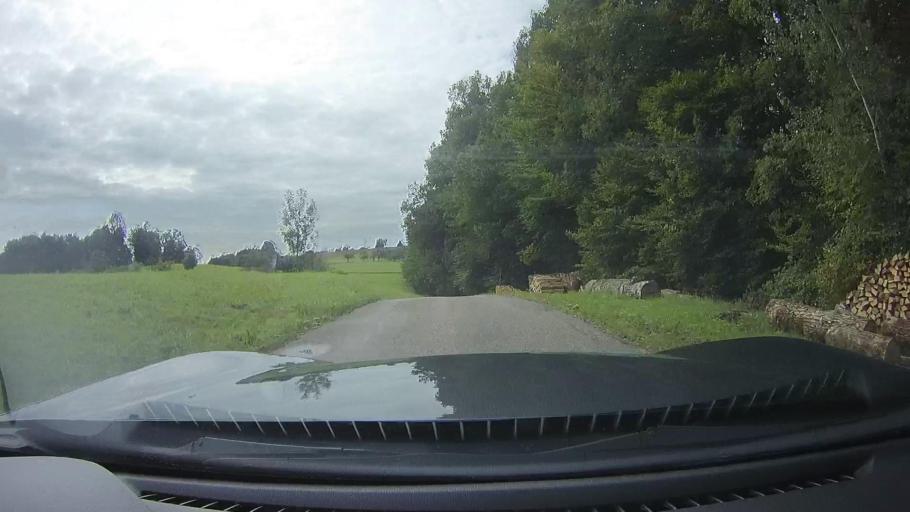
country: DE
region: Baden-Wuerttemberg
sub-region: Regierungsbezirk Stuttgart
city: Spiegelberg
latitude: 49.0364
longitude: 9.4620
